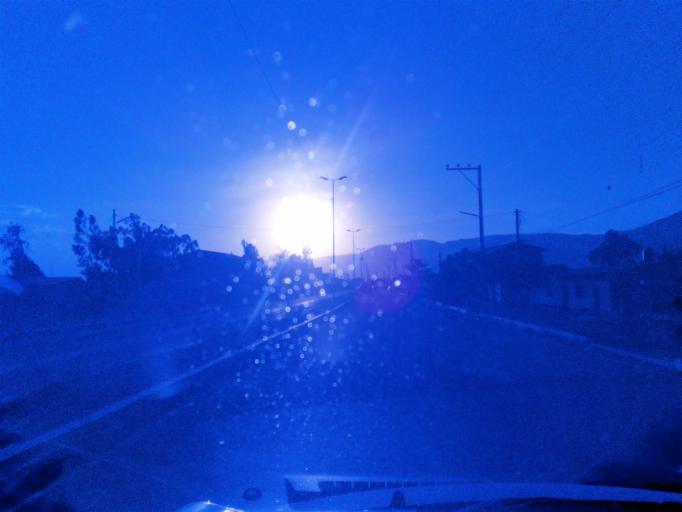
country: BO
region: Cochabamba
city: Punata
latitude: -17.5514
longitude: -65.8207
